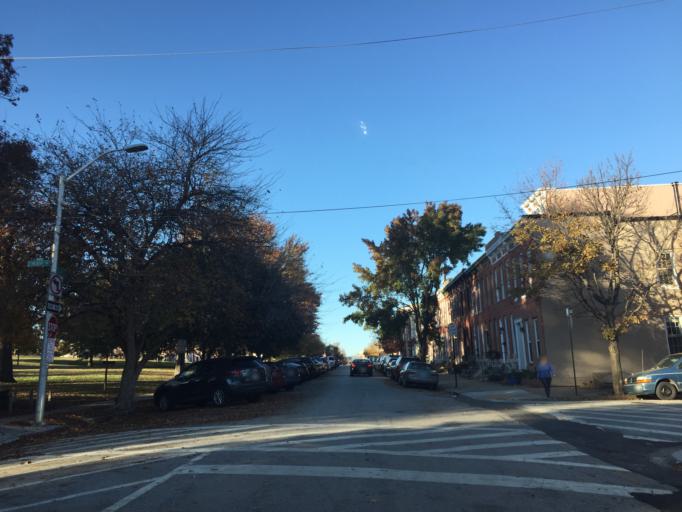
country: US
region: Maryland
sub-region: City of Baltimore
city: Baltimore
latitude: 39.2706
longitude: -76.6065
